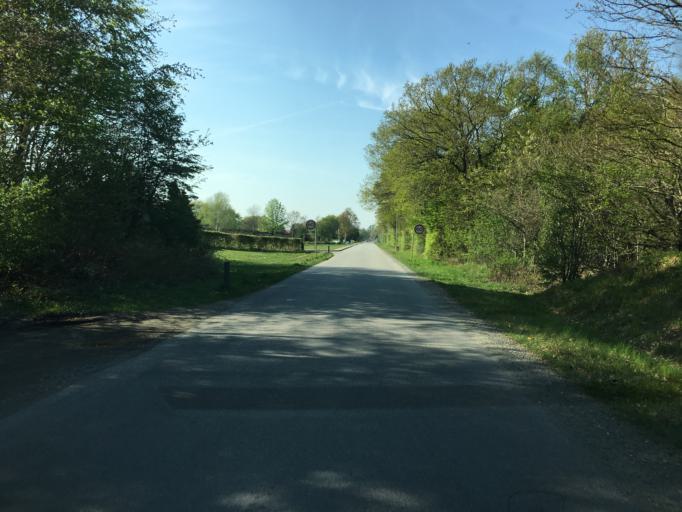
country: DK
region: South Denmark
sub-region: Haderslev Kommune
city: Vojens
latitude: 55.2434
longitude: 9.3185
